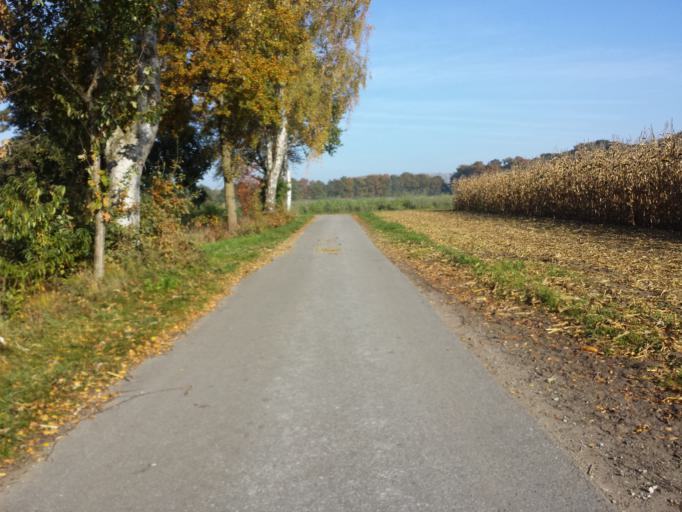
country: DE
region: North Rhine-Westphalia
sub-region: Regierungsbezirk Detmold
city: Guetersloh
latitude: 51.9308
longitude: 8.3375
